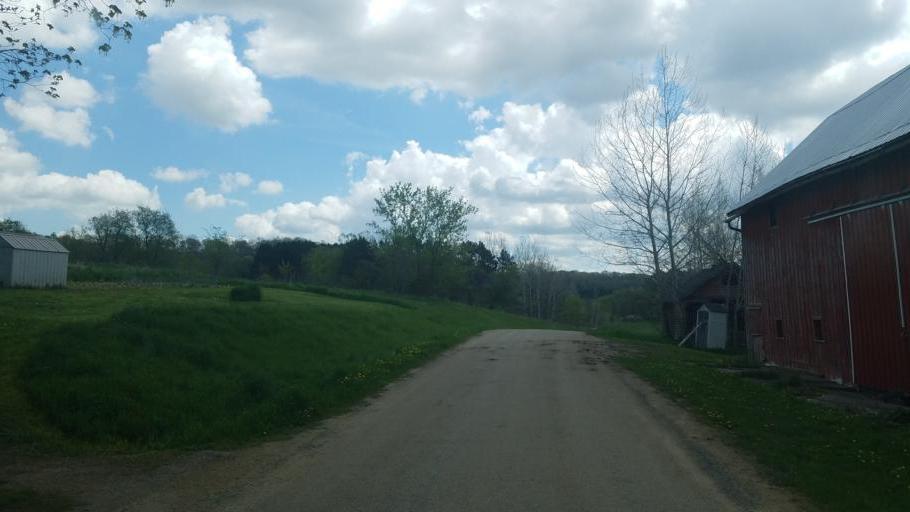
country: US
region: Wisconsin
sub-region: Vernon County
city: Hillsboro
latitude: 43.6097
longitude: -90.3512
